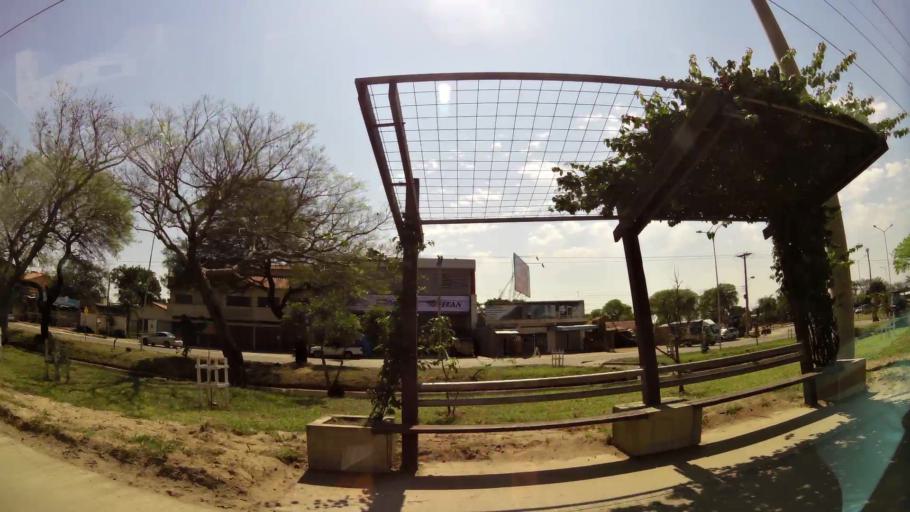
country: BO
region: Santa Cruz
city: Santa Cruz de la Sierra
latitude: -17.7524
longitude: -63.1928
